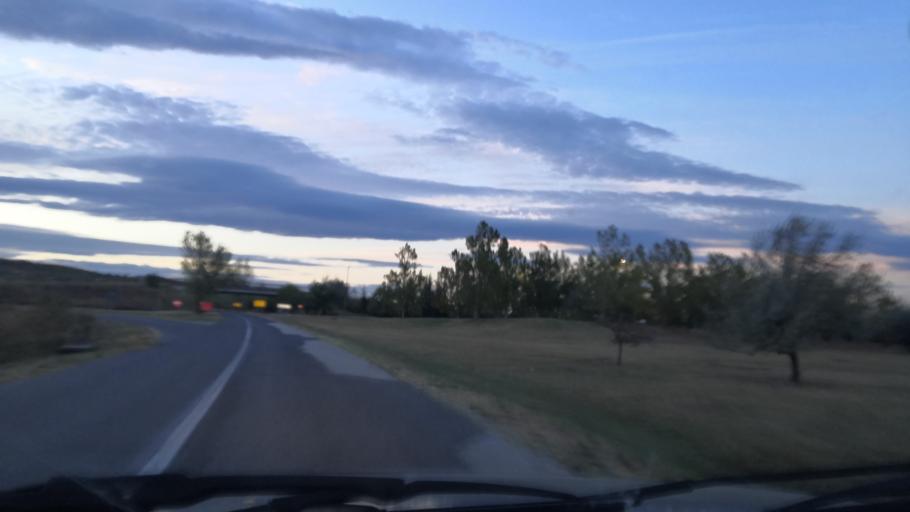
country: RO
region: Mehedinti
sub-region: Comuna Gogosu
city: Balta Verde
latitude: 44.2947
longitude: 22.5562
